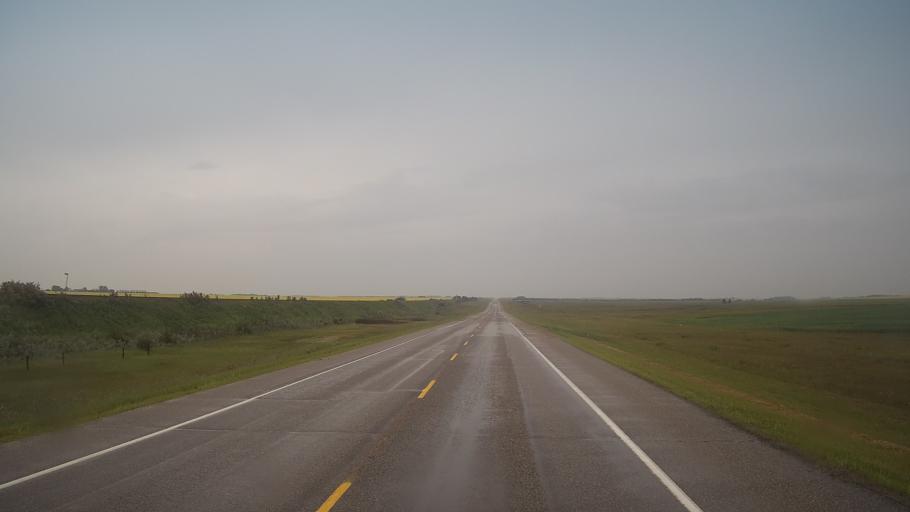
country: CA
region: Saskatchewan
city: Wilkie
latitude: 52.2133
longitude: -108.4974
